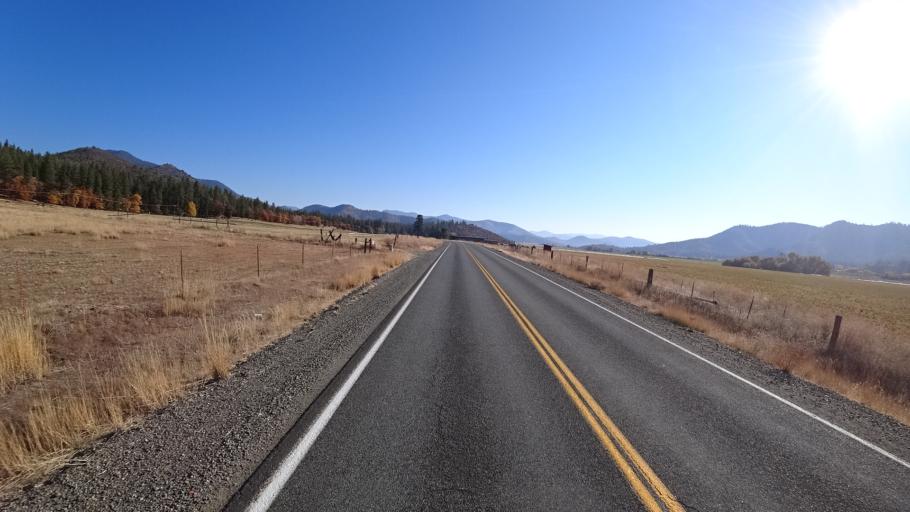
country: US
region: California
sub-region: Siskiyou County
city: Yreka
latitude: 41.6328
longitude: -122.9507
